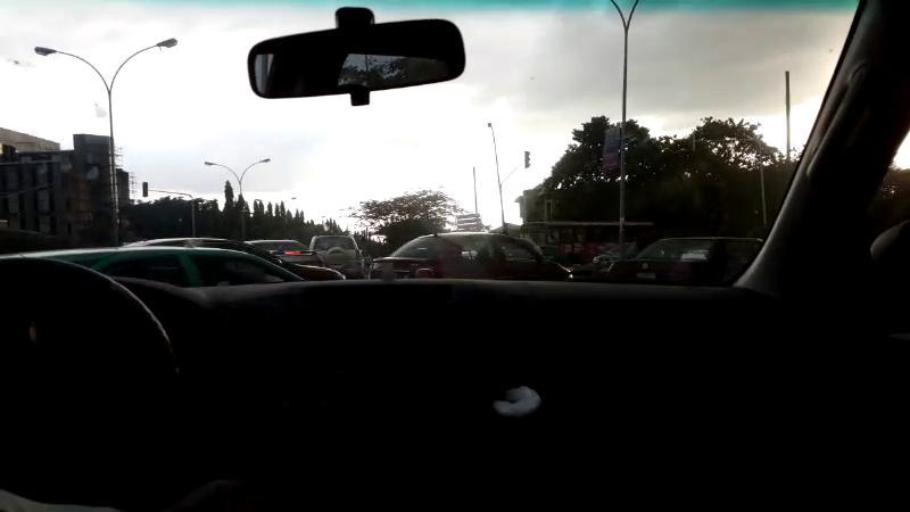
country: NG
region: Abuja Federal Capital Territory
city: Abuja
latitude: 9.0738
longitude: 7.4823
